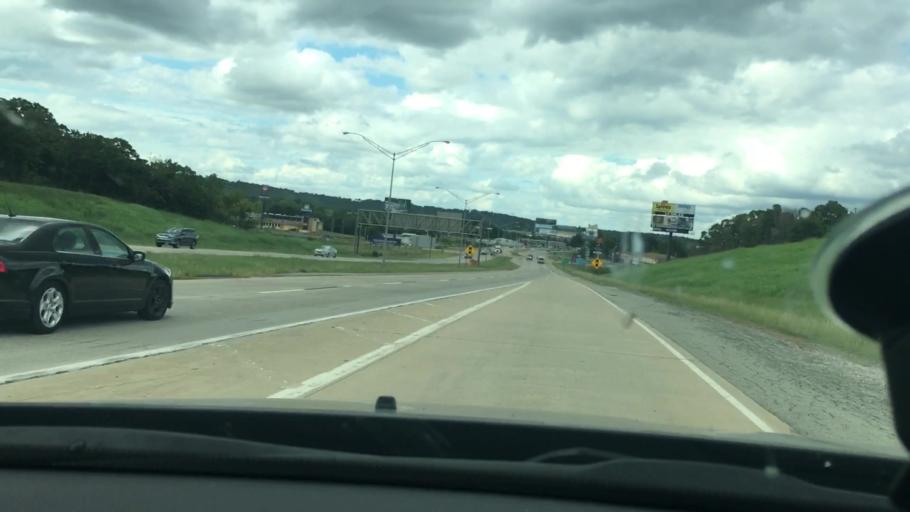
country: US
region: Oklahoma
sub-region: Okmulgee County
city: Henryetta
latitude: 35.4362
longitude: -95.9706
